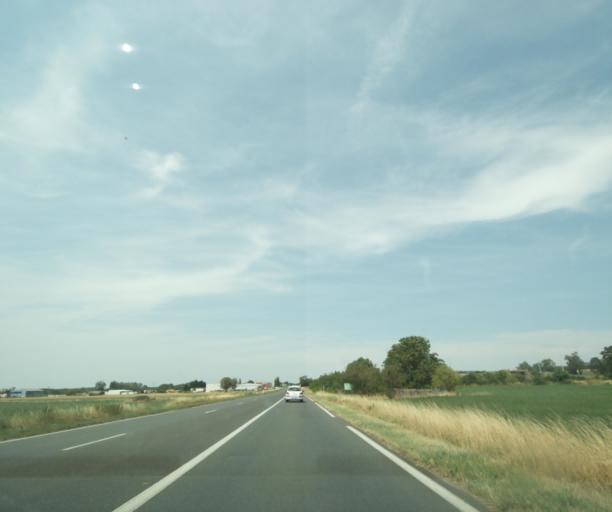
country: FR
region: Poitou-Charentes
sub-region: Departement de la Vienne
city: Les Ormes
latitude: 46.9561
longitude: 0.6076
